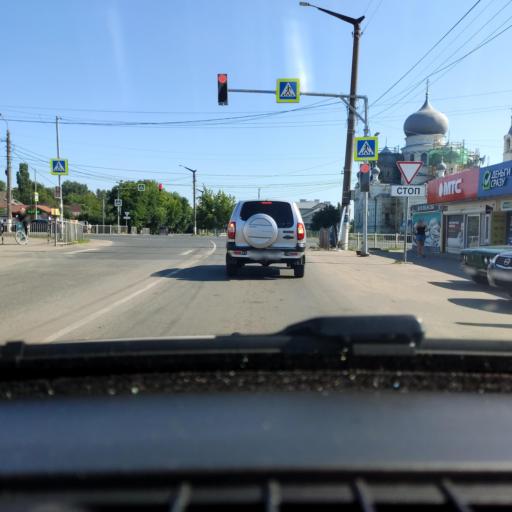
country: RU
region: Voronezj
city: Anna
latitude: 51.4904
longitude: 40.4374
